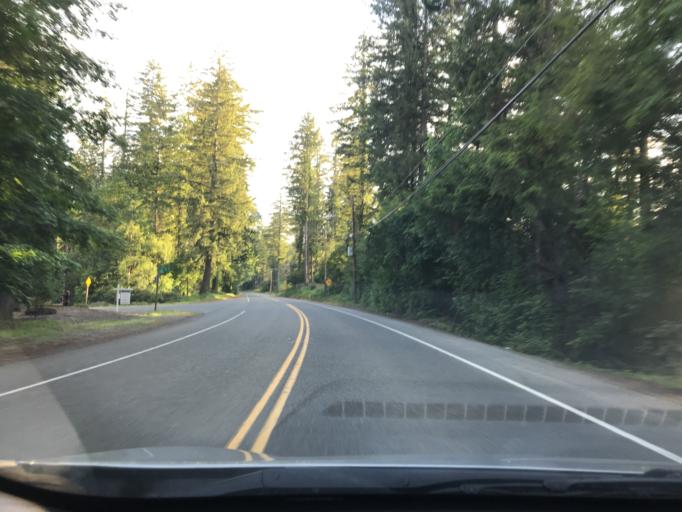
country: US
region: Washington
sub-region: King County
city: Black Diamond
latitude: 47.3104
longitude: -122.0430
